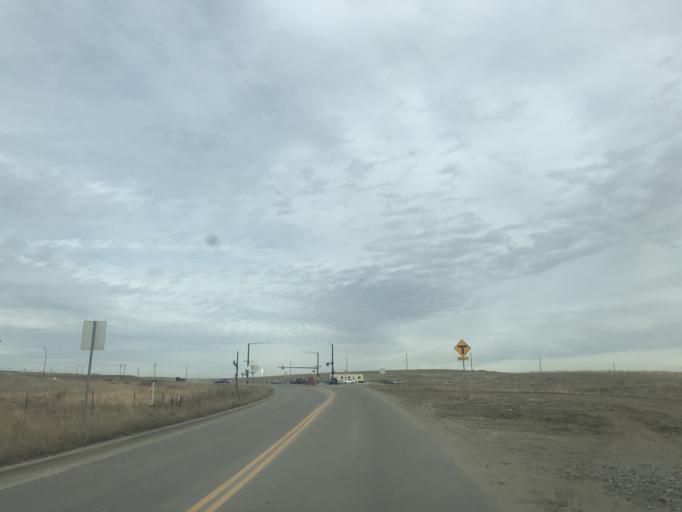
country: US
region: Colorado
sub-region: Douglas County
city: Meridian
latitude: 39.5214
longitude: -104.8616
